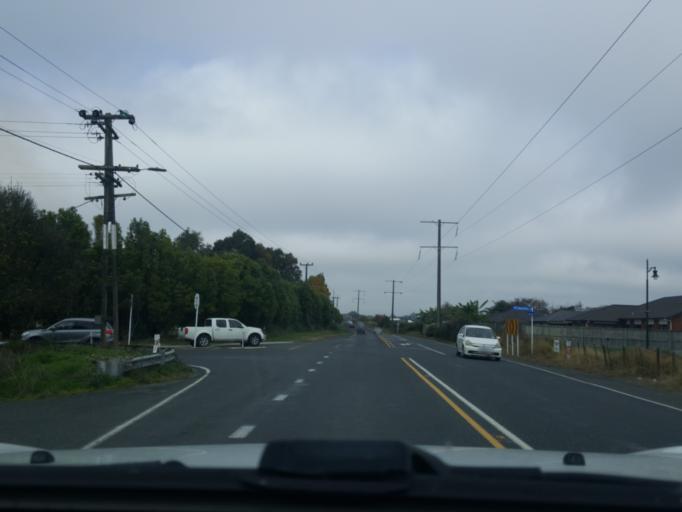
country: NZ
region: Waikato
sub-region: Hamilton City
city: Hamilton
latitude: -37.7386
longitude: 175.2890
